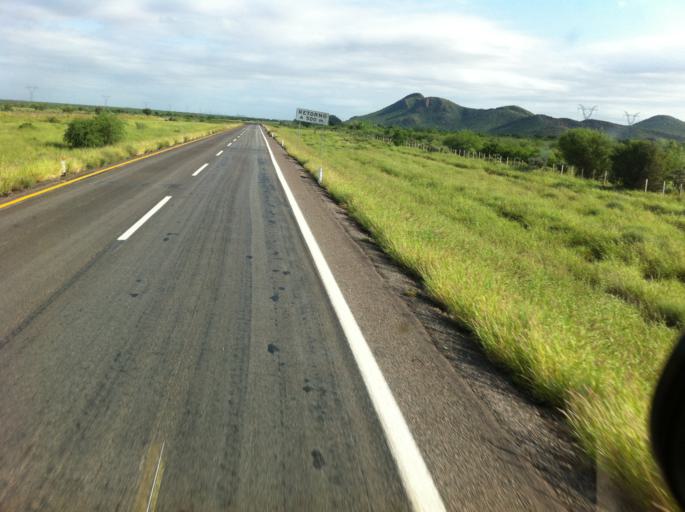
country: MX
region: Sonora
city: Hermosillo
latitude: 28.6106
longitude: -111.0172
